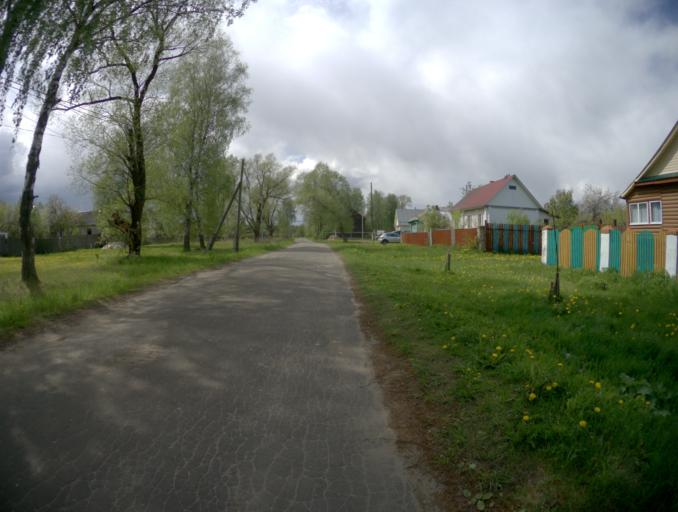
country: RU
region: Vladimir
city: Velikodvorskiy
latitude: 55.2411
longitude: 40.6630
